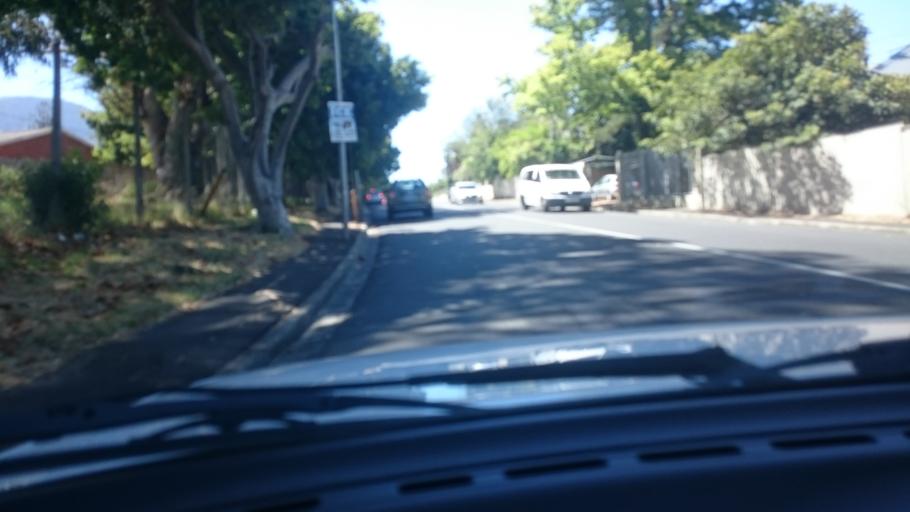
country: ZA
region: Western Cape
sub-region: City of Cape Town
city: Claremont
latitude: -34.0055
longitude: 18.4620
